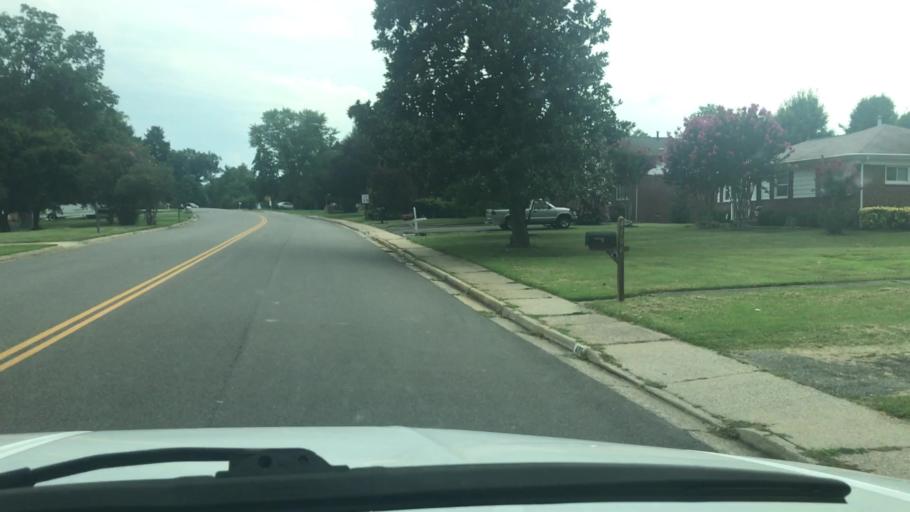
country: US
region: Virginia
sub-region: Henrico County
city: Laurel
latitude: 37.6452
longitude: -77.5421
